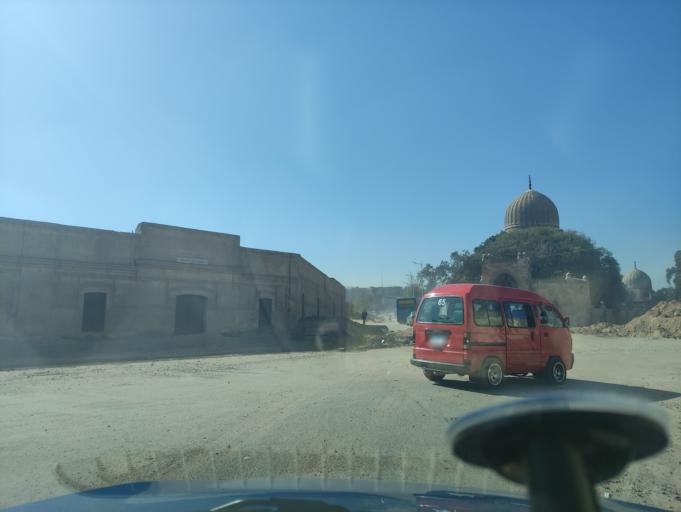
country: EG
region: Muhafazat al Qahirah
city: Cairo
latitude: 30.0529
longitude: 31.2803
